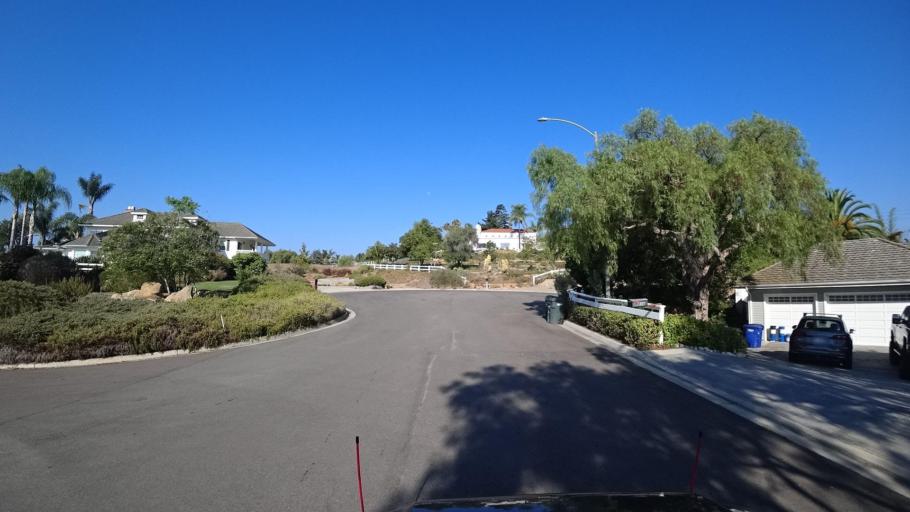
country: US
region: California
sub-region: San Diego County
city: Bonsall
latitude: 33.3285
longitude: -117.2514
